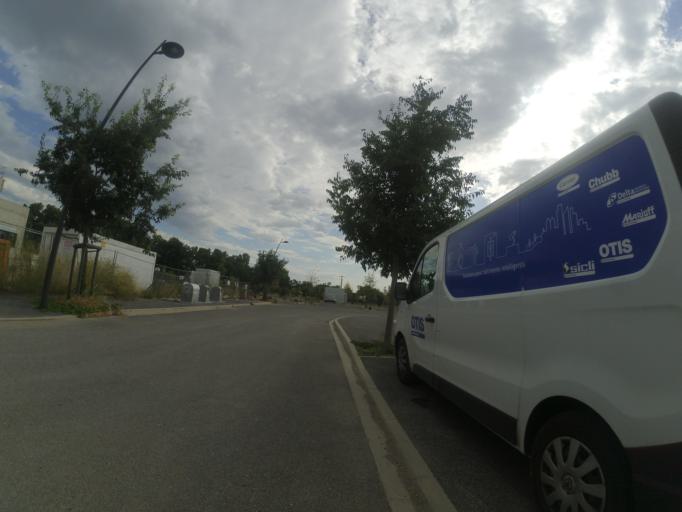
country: FR
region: Languedoc-Roussillon
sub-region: Departement des Pyrenees-Orientales
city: Toulouges
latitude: 42.6755
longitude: 2.8259
